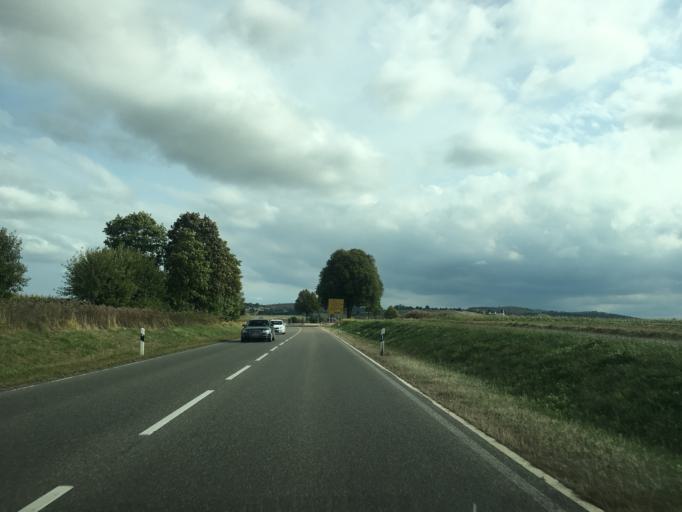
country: DE
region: Baden-Wuerttemberg
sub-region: Tuebingen Region
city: Sankt Johann
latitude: 48.3965
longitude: 9.2810
